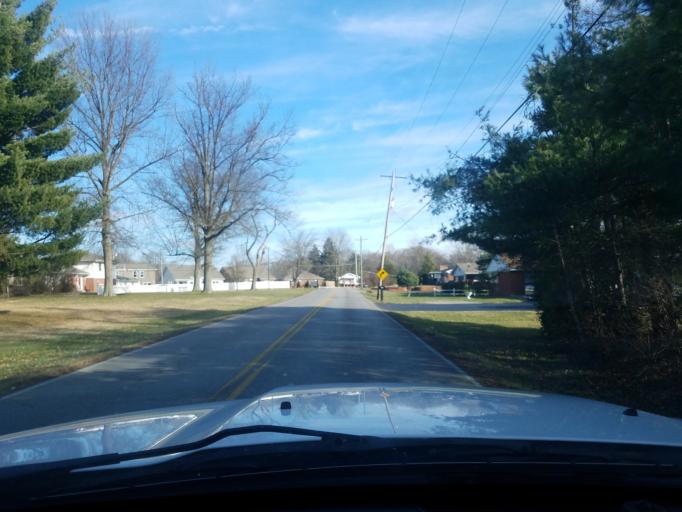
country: US
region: Indiana
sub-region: Clark County
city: Clarksville
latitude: 38.3159
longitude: -85.7753
